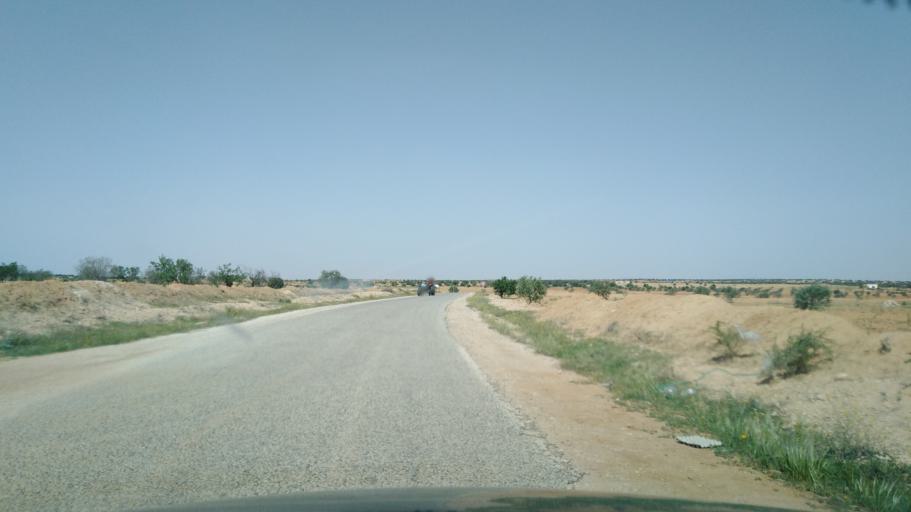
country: TN
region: Safaqis
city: Bi'r `Ali Bin Khalifah
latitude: 34.6780
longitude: 10.4171
